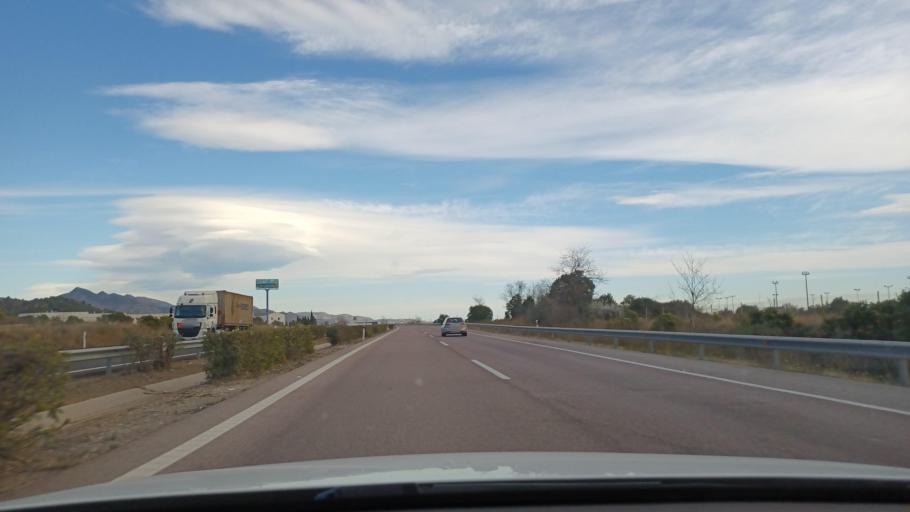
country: ES
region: Valencia
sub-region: Provincia de Castello
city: Castello de la Plana
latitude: 39.9969
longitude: -0.0759
